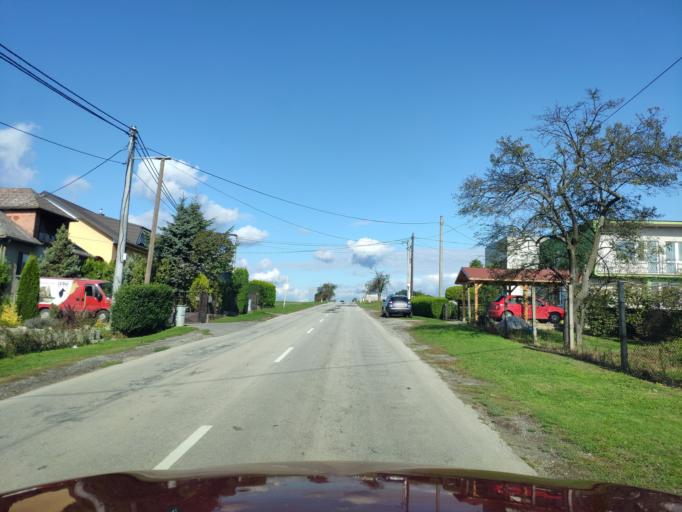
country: SK
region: Presovsky
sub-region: Okres Presov
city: Presov
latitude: 48.8780
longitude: 21.2696
